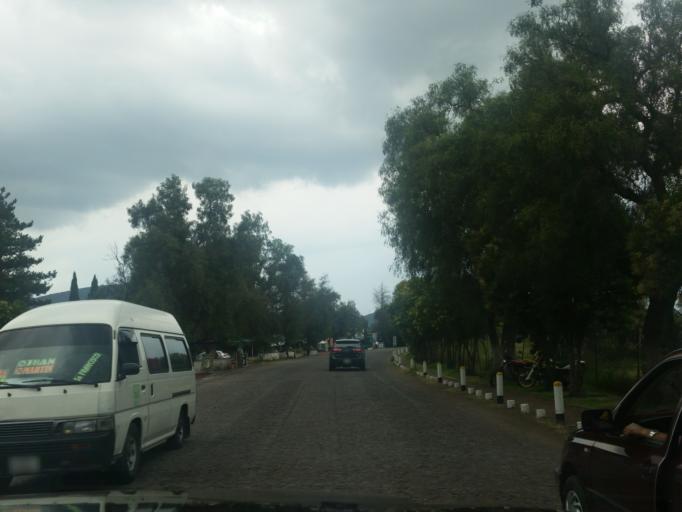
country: MX
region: Mexico
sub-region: Teotihuacan
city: Teotihuacan de Arista
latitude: 19.6812
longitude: -98.8438
